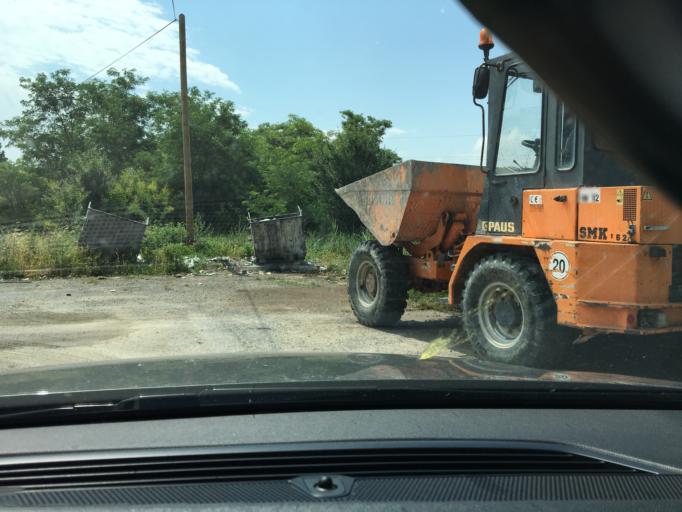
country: MK
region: Sveti Nikole
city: Sveti Nikole
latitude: 41.8698
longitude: 21.9475
